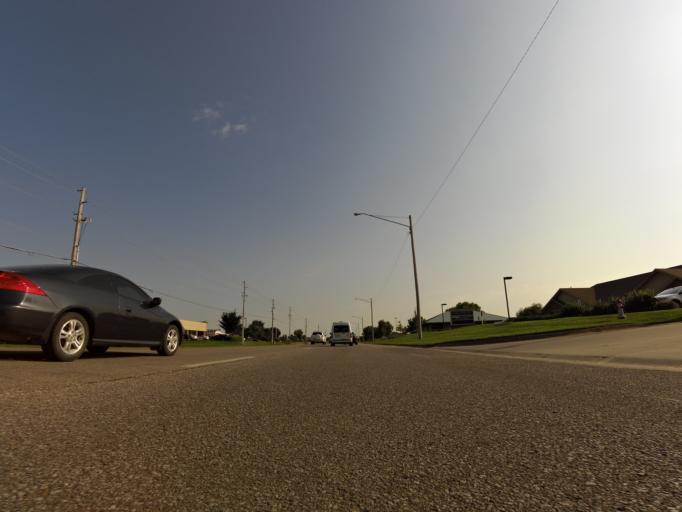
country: US
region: Kansas
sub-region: Sedgwick County
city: Maize
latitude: 37.7479
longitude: -97.4263
